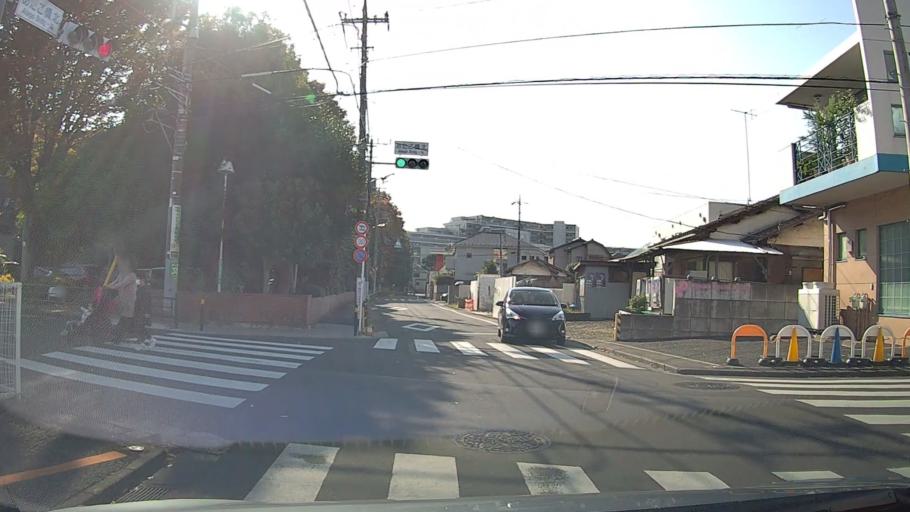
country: JP
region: Tokyo
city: Musashino
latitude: 35.7335
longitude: 139.5904
